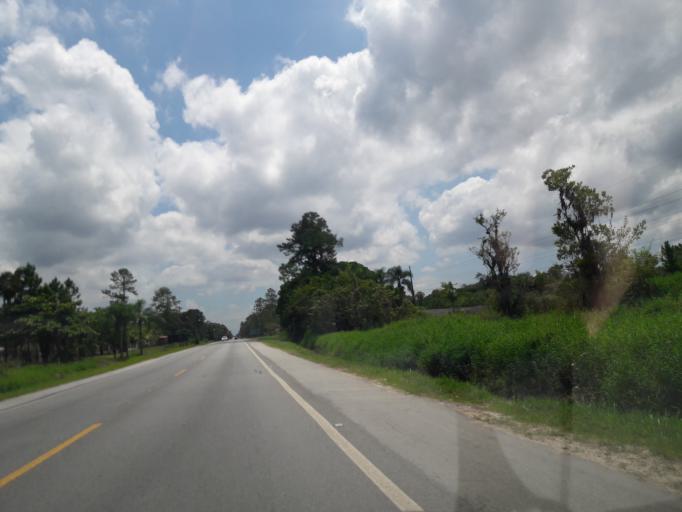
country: BR
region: Parana
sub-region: Pontal Do Parana
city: Pontal do Parana
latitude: -25.6414
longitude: -48.5329
